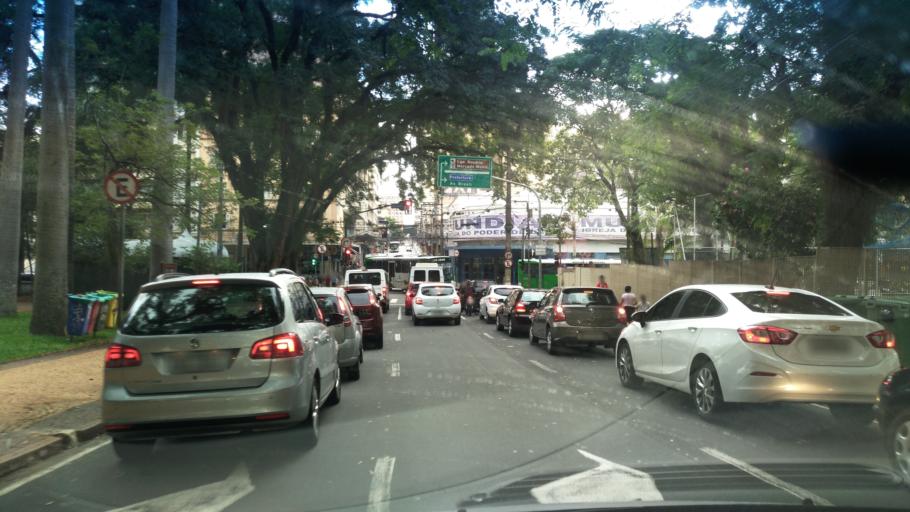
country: BR
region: Sao Paulo
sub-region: Campinas
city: Campinas
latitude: -22.9027
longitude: -47.0566
